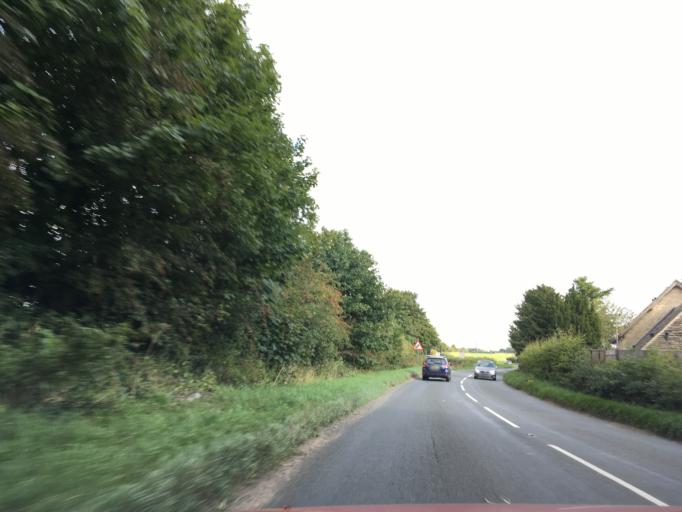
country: GB
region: England
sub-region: Gloucestershire
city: Nailsworth
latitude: 51.6495
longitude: -2.2267
